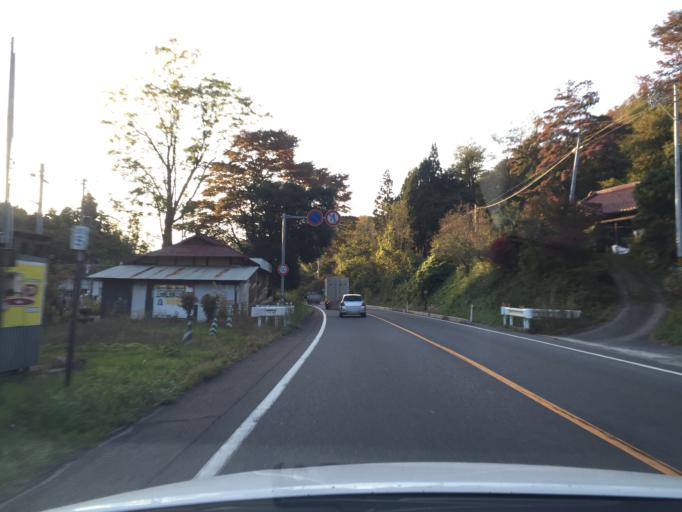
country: JP
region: Fukushima
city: Sukagawa
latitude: 37.3138
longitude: 140.4687
